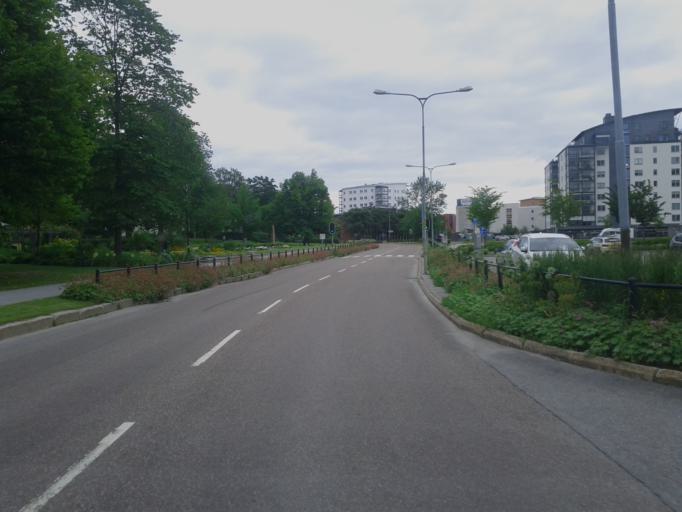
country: SE
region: Vaesternorrland
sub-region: OErnskoeldsviks Kommun
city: Ornskoldsvik
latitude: 63.2876
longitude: 18.7146
